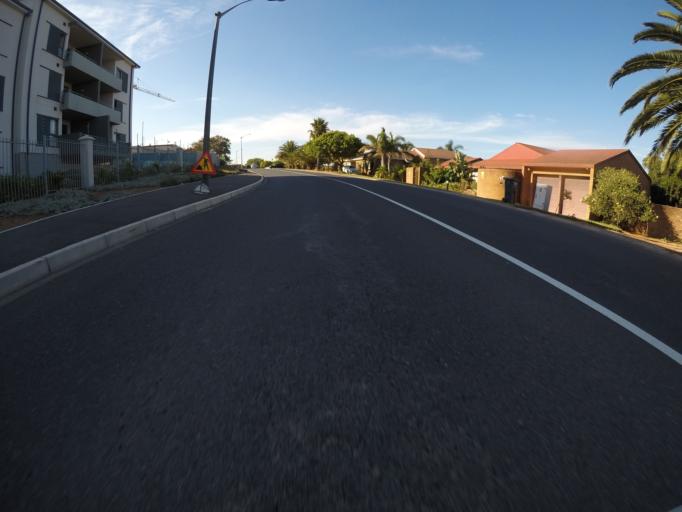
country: ZA
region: Western Cape
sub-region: City of Cape Town
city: Kraaifontein
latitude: -33.8775
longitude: 18.6458
